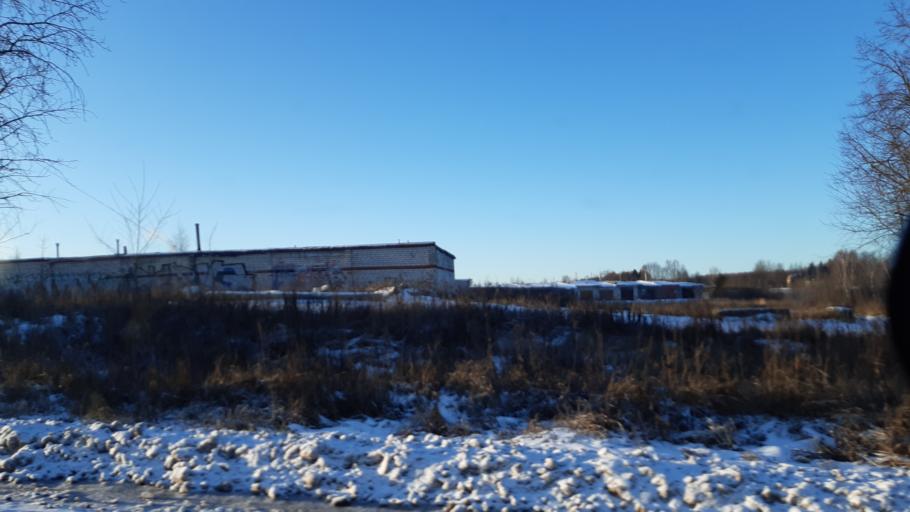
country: RU
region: Moskovskaya
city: Skoropuskovskiy
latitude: 56.3427
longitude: 38.1677
